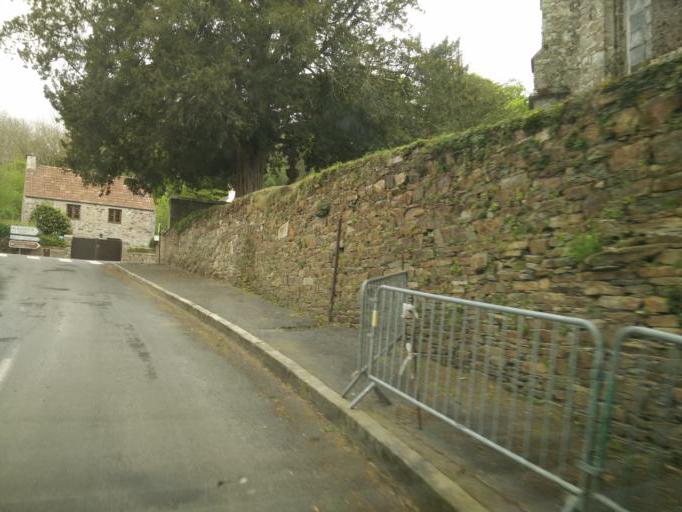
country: FR
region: Brittany
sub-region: Departement des Cotes-d'Armor
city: Lannion
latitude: 48.7358
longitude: -3.4825
